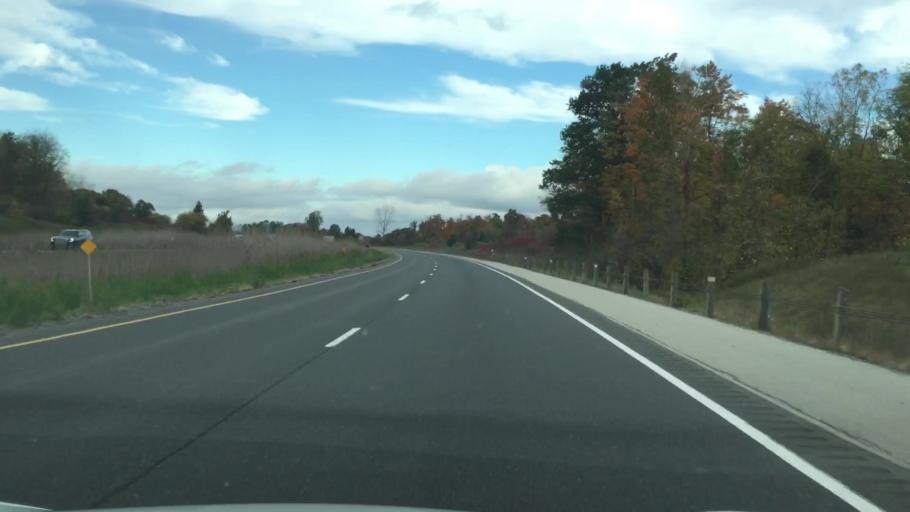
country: CA
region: Ontario
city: Delaware
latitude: 42.8978
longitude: -81.3752
